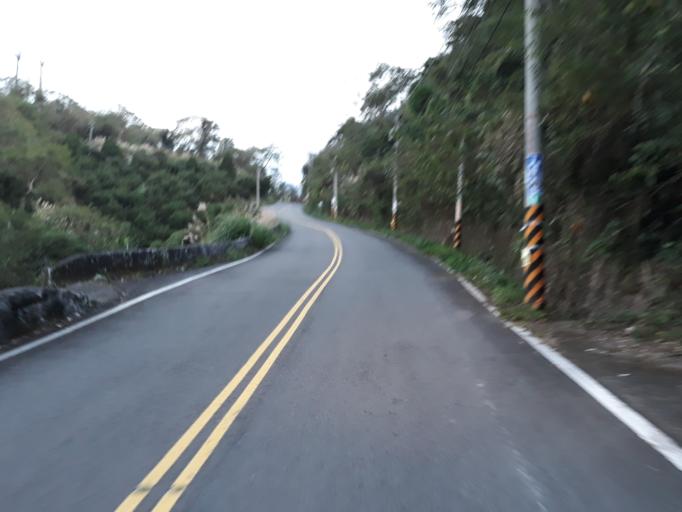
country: TW
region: Taiwan
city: Fengyuan
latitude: 24.3617
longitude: 120.8679
